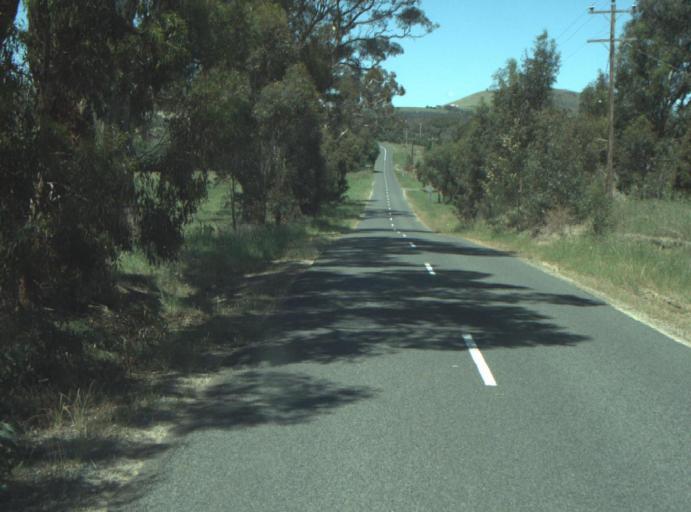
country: AU
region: Victoria
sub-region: Greater Geelong
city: Lara
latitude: -37.8505
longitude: 144.2815
